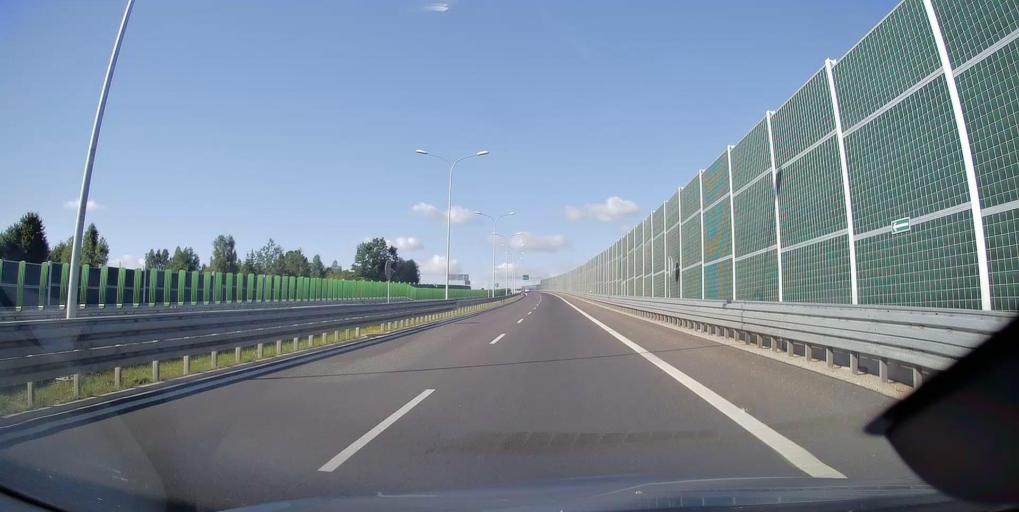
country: PL
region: Swietokrzyskie
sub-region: Powiat skarzyski
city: Skarzysko-Kamienna
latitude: 51.1110
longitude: 20.8465
